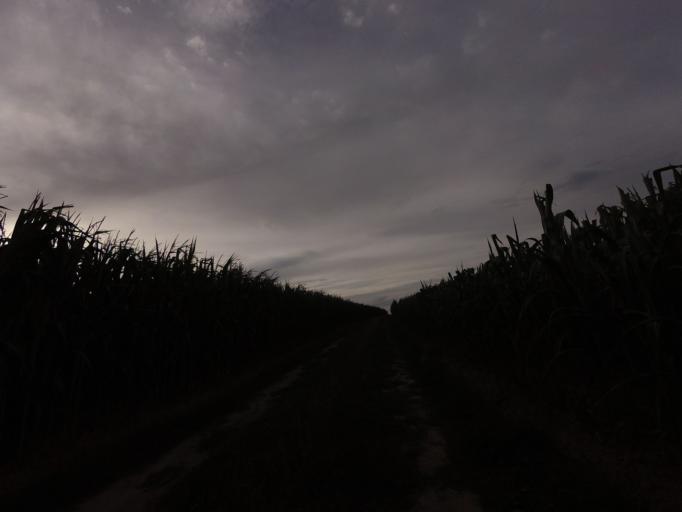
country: BE
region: Flanders
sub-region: Provincie Vlaams-Brabant
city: Grimbergen
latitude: 50.9647
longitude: 4.3657
